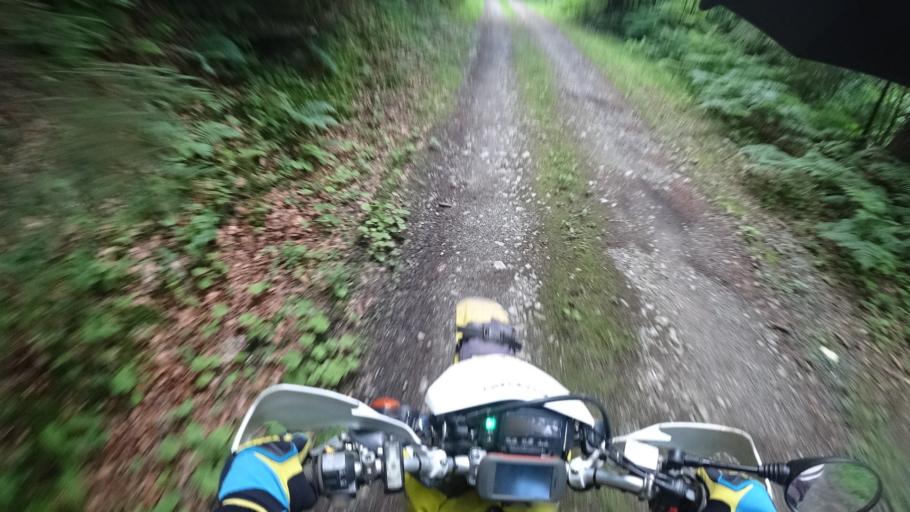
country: SI
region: Osilnica
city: Osilnica
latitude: 45.4633
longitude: 14.7094
